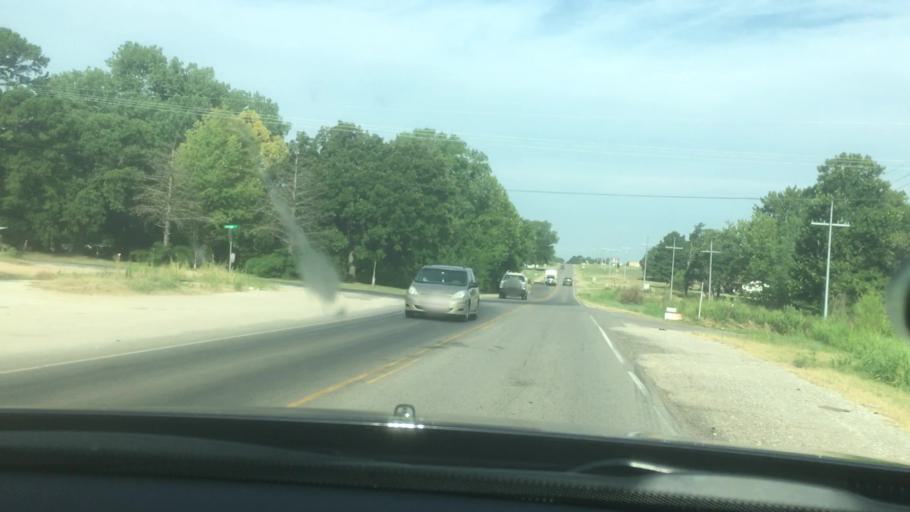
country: US
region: Oklahoma
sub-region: Pontotoc County
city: Ada
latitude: 34.7821
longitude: -96.7743
